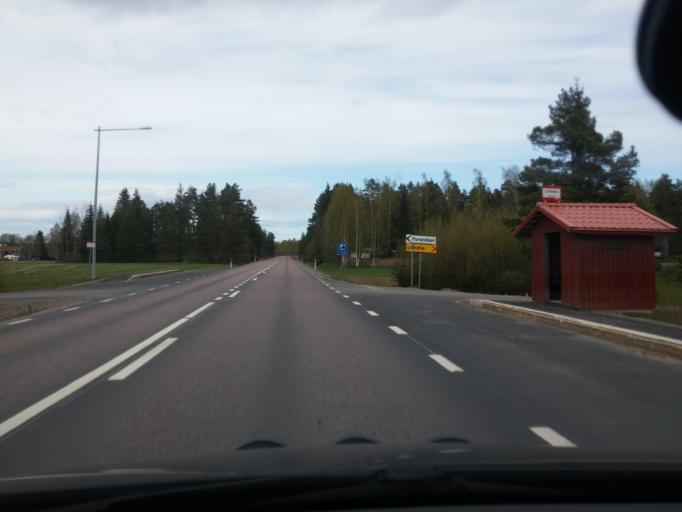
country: SE
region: Gaevleborg
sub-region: Ljusdals Kommun
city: Ljusdal
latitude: 61.8196
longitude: 16.0253
